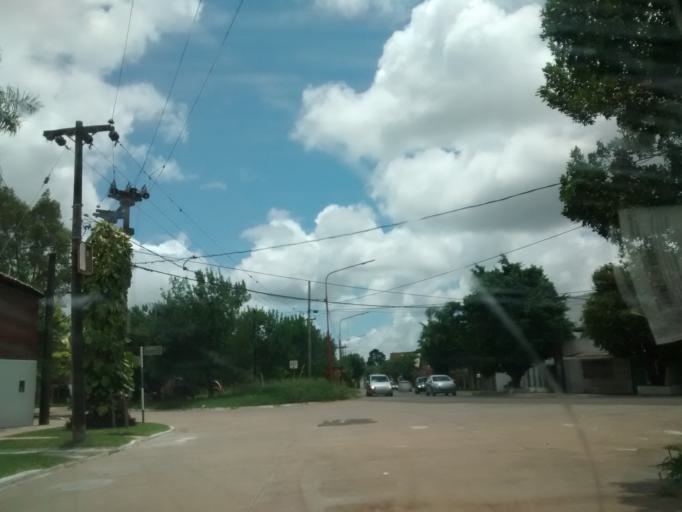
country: AR
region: Chaco
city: Resistencia
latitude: -27.4338
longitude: -58.9826
